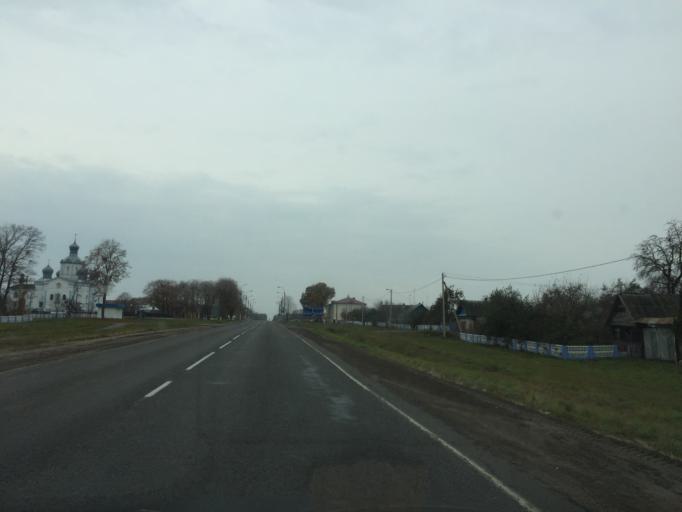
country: BY
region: Gomel
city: Dowsk
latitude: 53.1595
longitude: 30.4647
